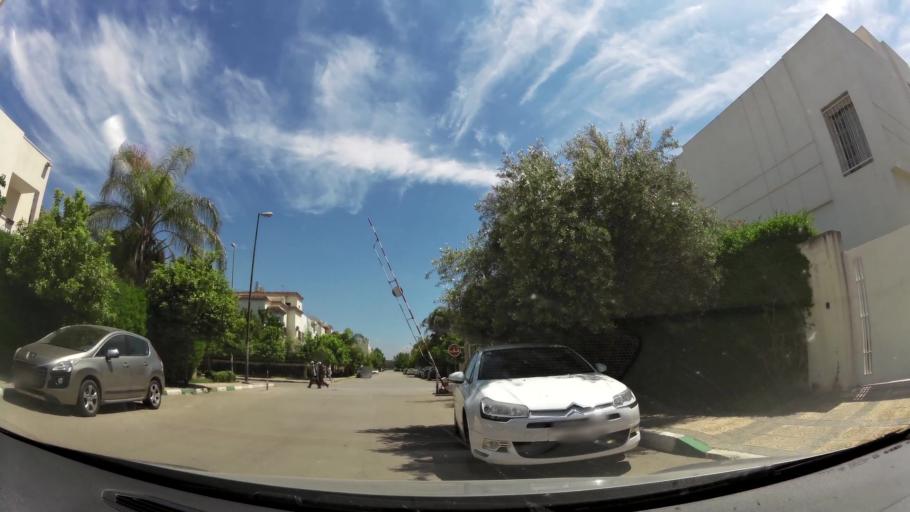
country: MA
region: Fes-Boulemane
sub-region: Fes
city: Fes
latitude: 34.0065
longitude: -4.9904
